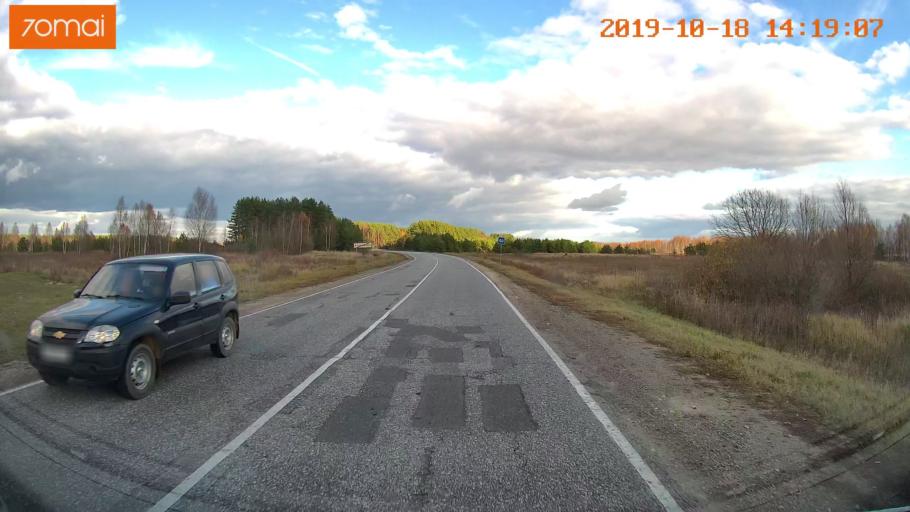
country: RU
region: Rjazan
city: Tuma
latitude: 55.1402
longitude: 40.4037
